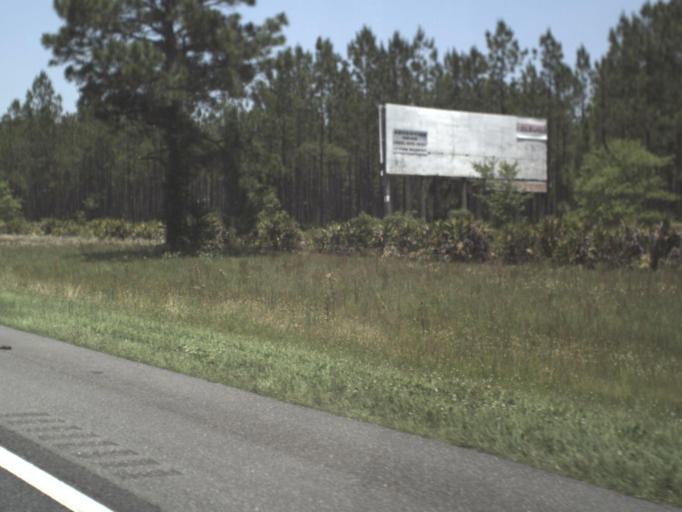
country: US
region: Florida
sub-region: Baker County
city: Macclenny
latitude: 30.2429
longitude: -82.3104
